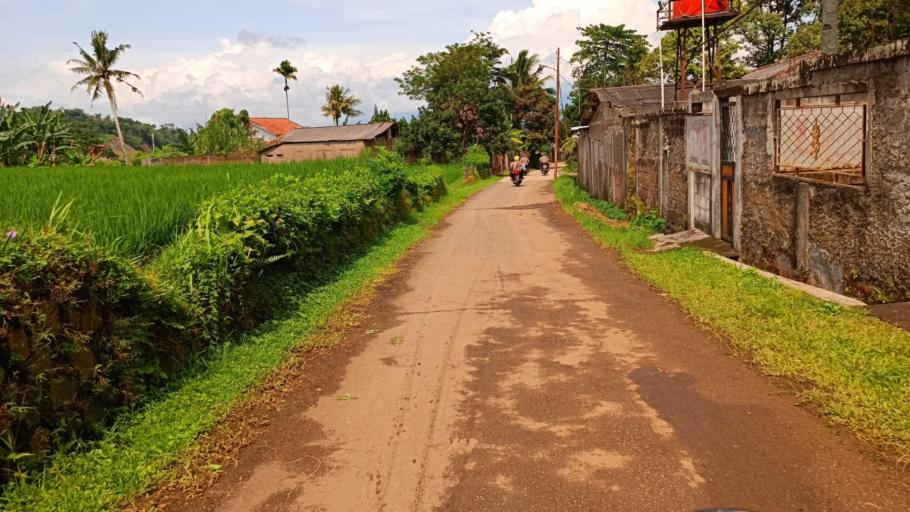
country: ID
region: West Java
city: Caringin
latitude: -6.6548
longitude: 106.8888
